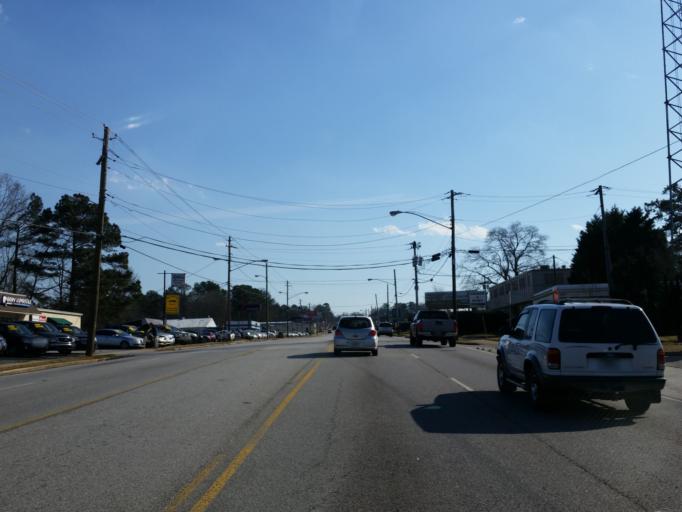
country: US
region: Georgia
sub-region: Spalding County
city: Experiment
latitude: 33.2559
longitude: -84.2882
